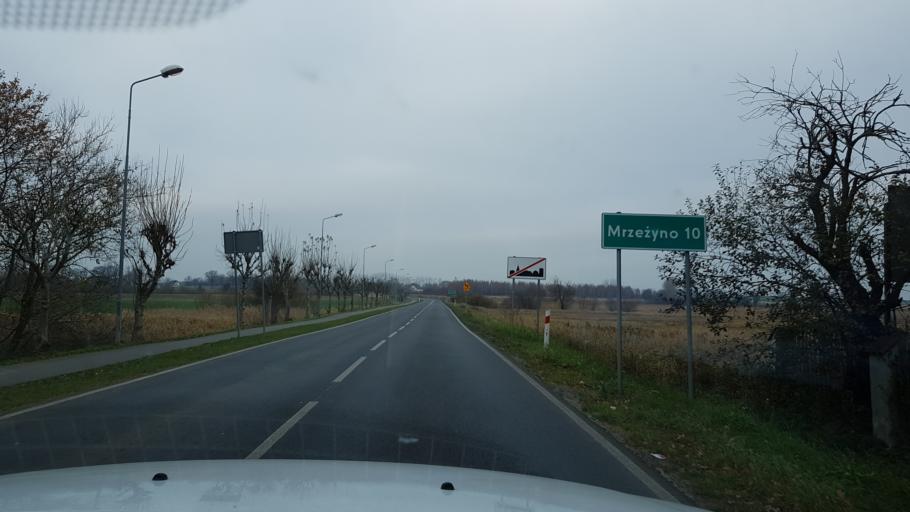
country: PL
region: West Pomeranian Voivodeship
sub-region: Powiat gryficki
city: Trzebiatow
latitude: 54.0658
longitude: 15.2619
